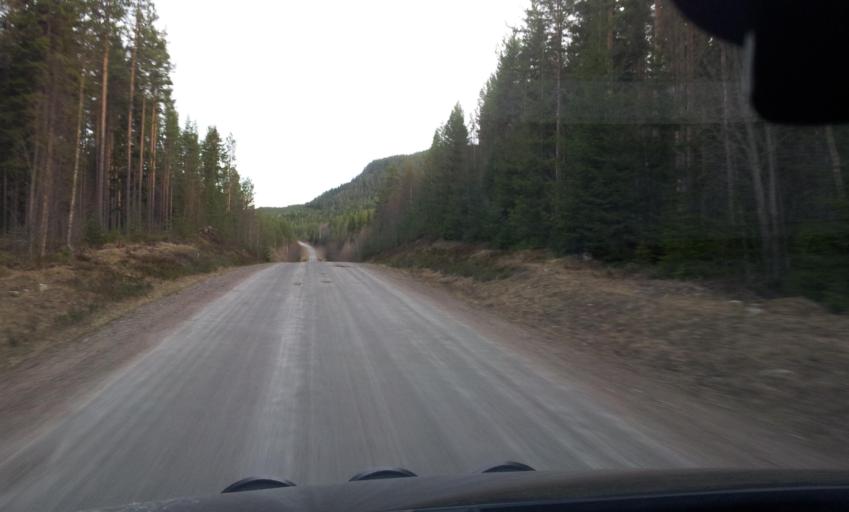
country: SE
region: Gaevleborg
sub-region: Ljusdals Kommun
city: Farila
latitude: 62.0386
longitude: 15.8216
